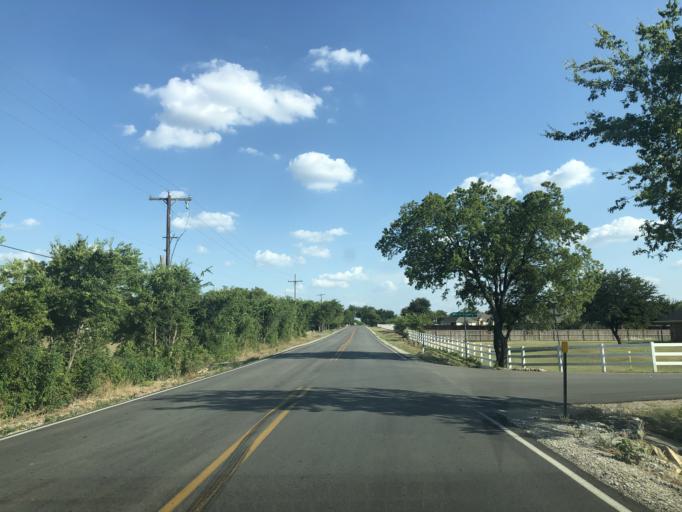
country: US
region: Texas
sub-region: Tarrant County
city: Eagle Mountain
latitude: 32.8957
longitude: -97.3972
